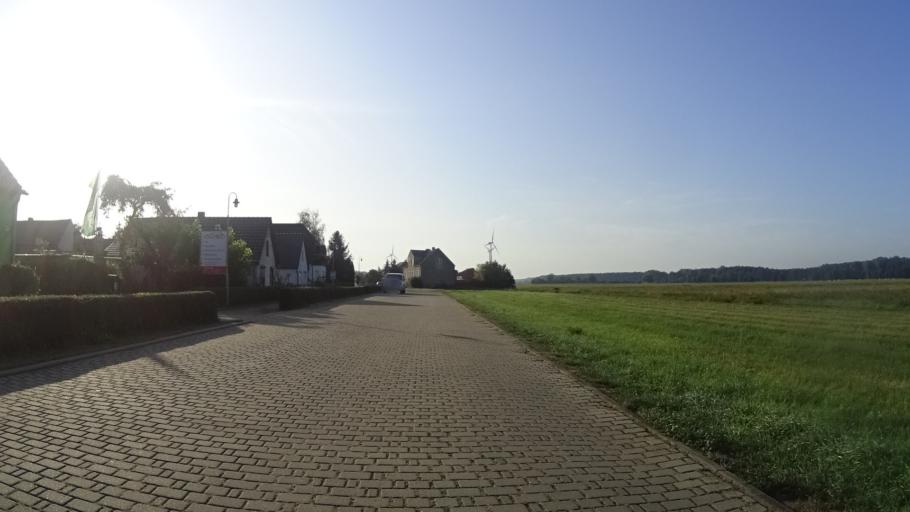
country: DE
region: Brandenburg
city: Kasel-Golzig
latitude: 51.9882
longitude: 13.6988
